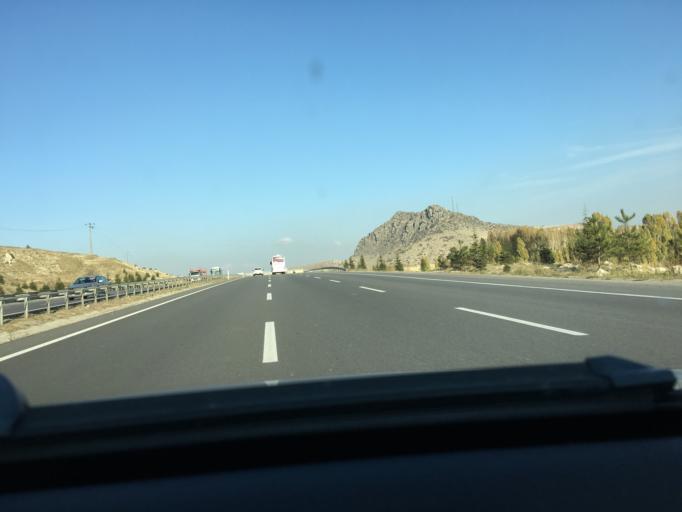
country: TR
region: Ankara
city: Temelli
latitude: 39.7676
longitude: 32.4849
